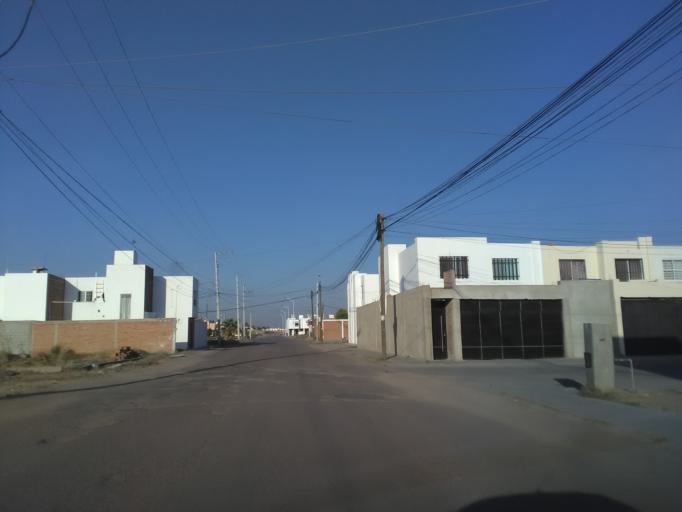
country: MX
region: Durango
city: Victoria de Durango
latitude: 24.0608
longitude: -104.6190
